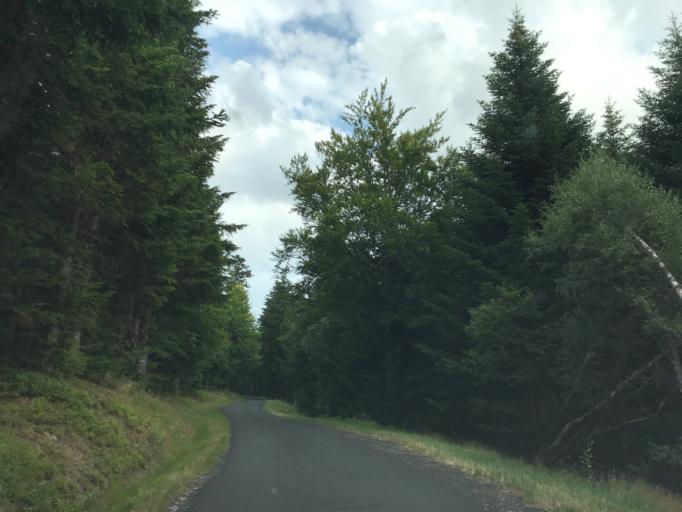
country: FR
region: Rhone-Alpes
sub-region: Departement de la Loire
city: Noiretable
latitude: 45.7669
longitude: 3.7254
